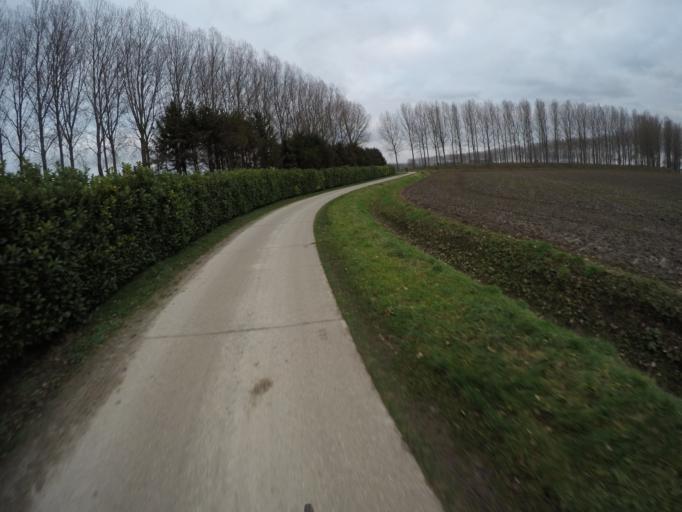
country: BE
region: Flanders
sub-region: Provincie Oost-Vlaanderen
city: Sint-Gillis-Waas
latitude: 51.2530
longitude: 4.1153
